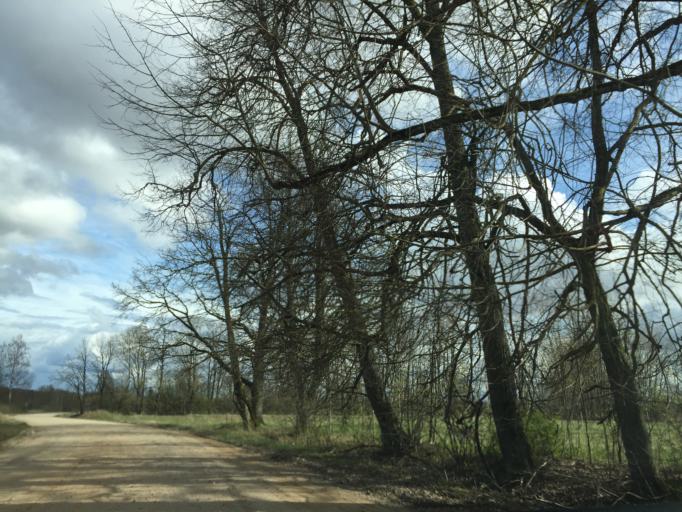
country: LV
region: Limbazu Rajons
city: Limbazi
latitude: 57.6147
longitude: 24.7214
